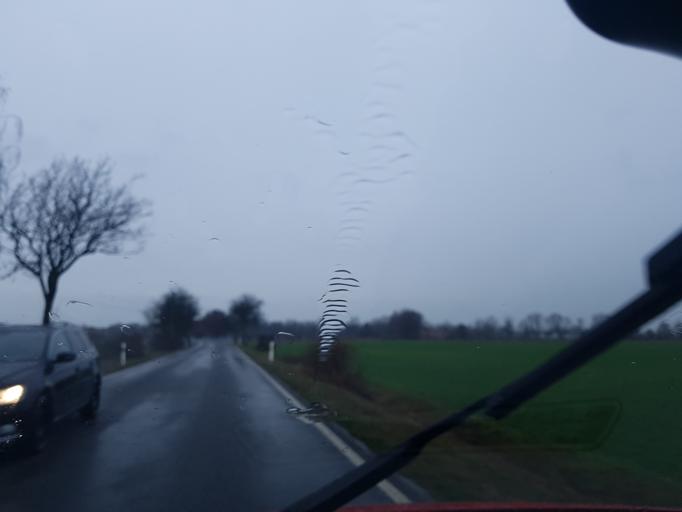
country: DE
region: Brandenburg
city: Schilda
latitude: 51.6128
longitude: 13.3186
